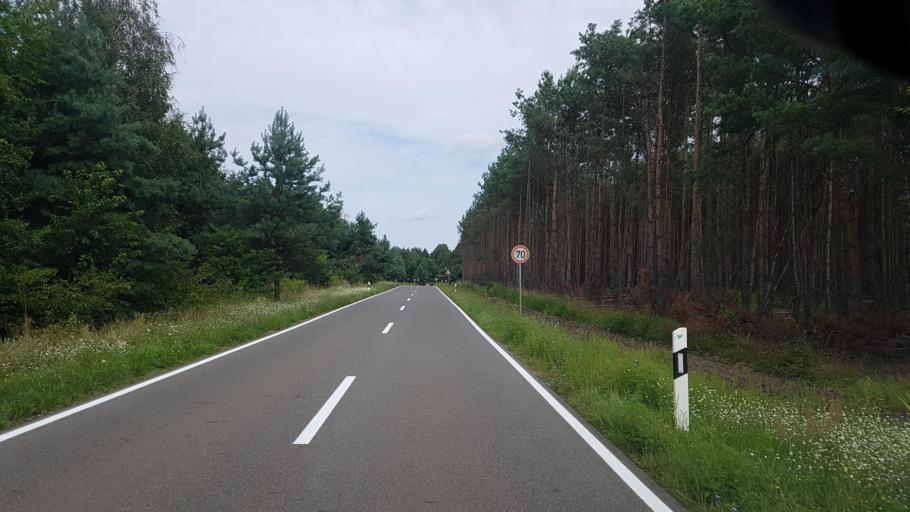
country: DE
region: Brandenburg
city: Spremberg
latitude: 51.6158
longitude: 14.3425
